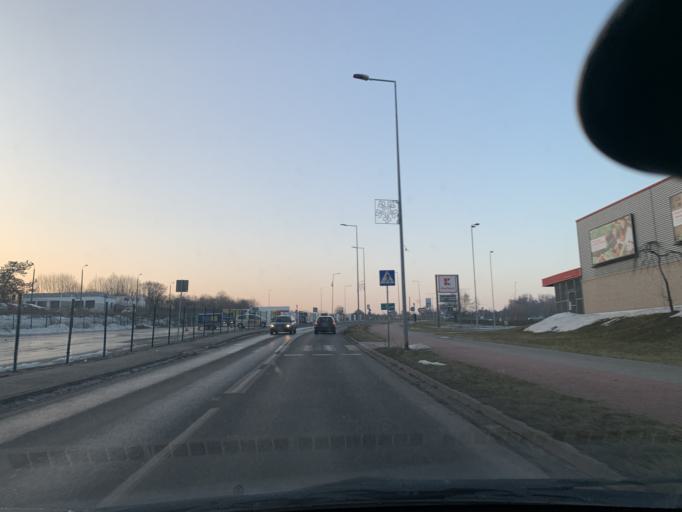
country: PL
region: Silesian Voivodeship
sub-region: Powiat tarnogorski
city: Radzionkow
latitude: 50.3985
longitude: 18.8932
